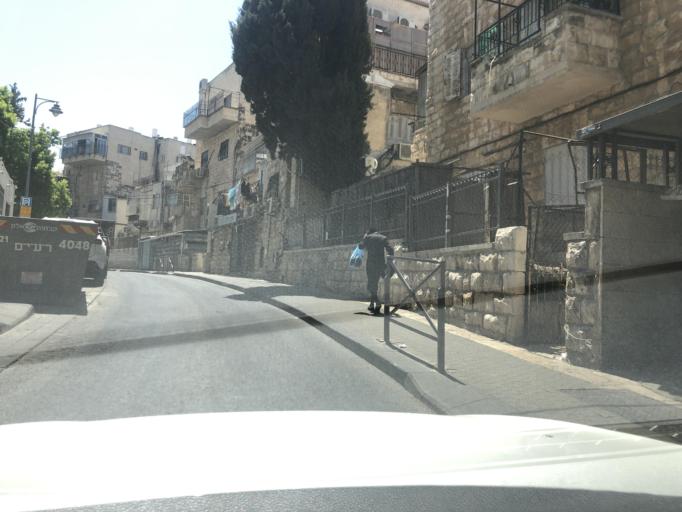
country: IL
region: Jerusalem
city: West Jerusalem
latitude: 31.7927
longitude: 35.2152
